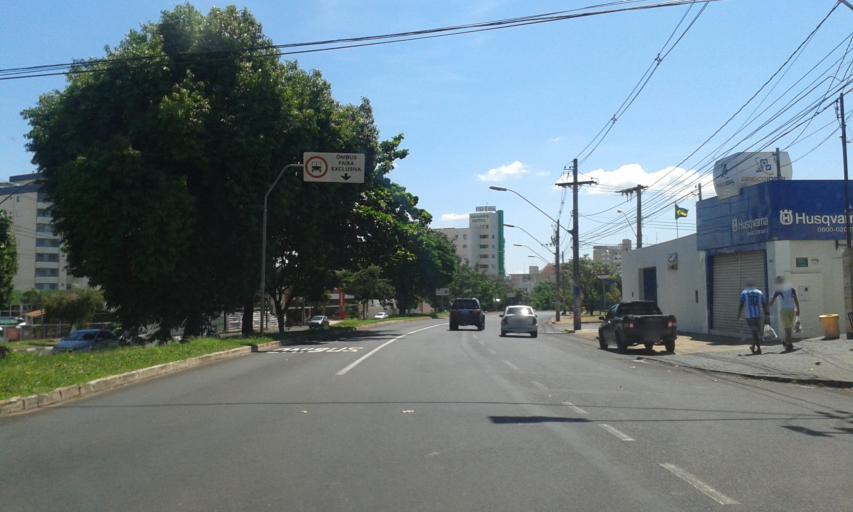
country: BR
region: Minas Gerais
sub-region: Uberlandia
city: Uberlandia
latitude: -18.9216
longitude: -48.2626
